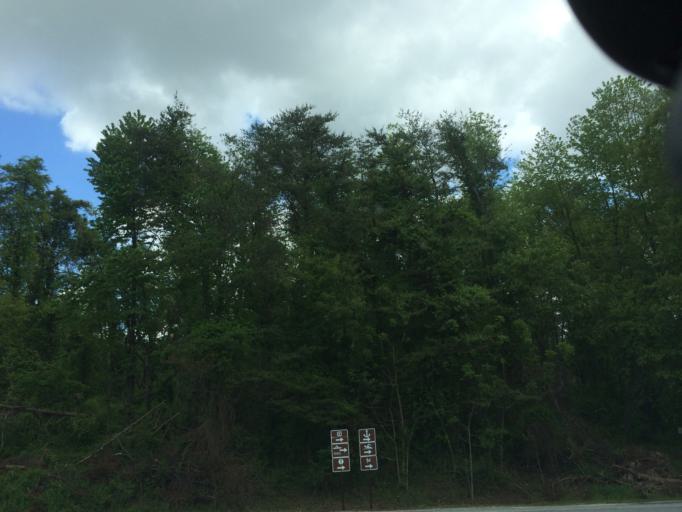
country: US
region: Pennsylvania
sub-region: York County
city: Parkville
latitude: 39.7894
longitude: -76.8895
